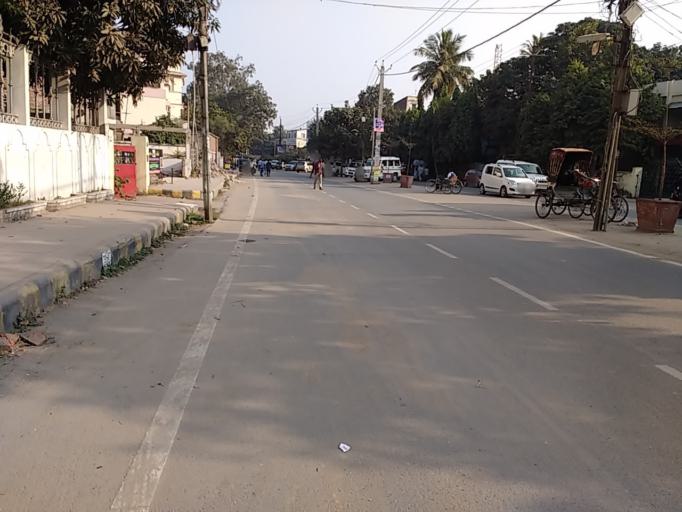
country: IN
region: Bihar
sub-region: Patna
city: Patna
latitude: 25.6122
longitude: 85.1153
